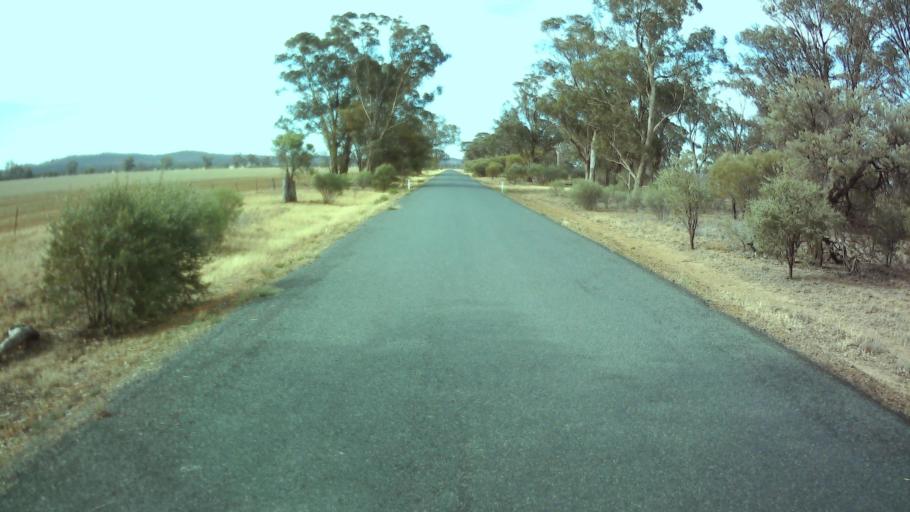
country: AU
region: New South Wales
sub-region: Weddin
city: Grenfell
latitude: -33.8642
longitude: 147.8593
